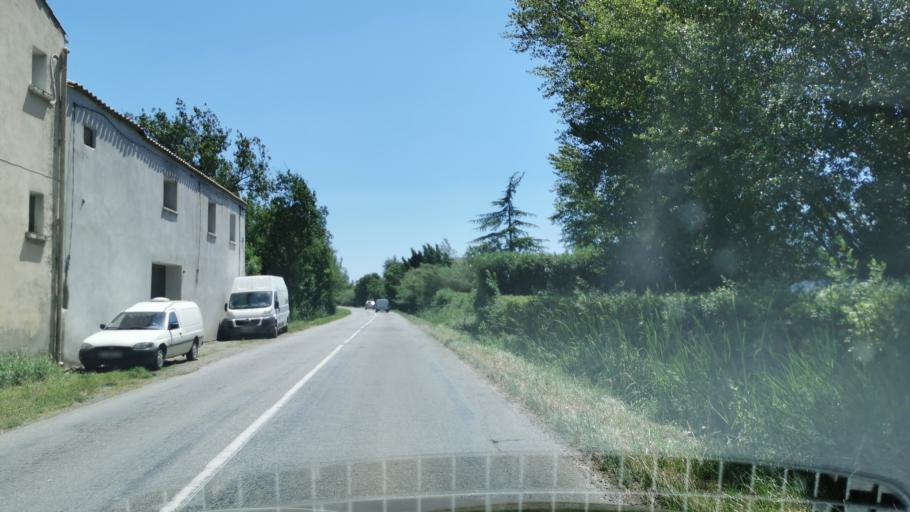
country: FR
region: Languedoc-Roussillon
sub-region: Departement de l'Aude
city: Narbonne
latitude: 43.2053
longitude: 3.0115
